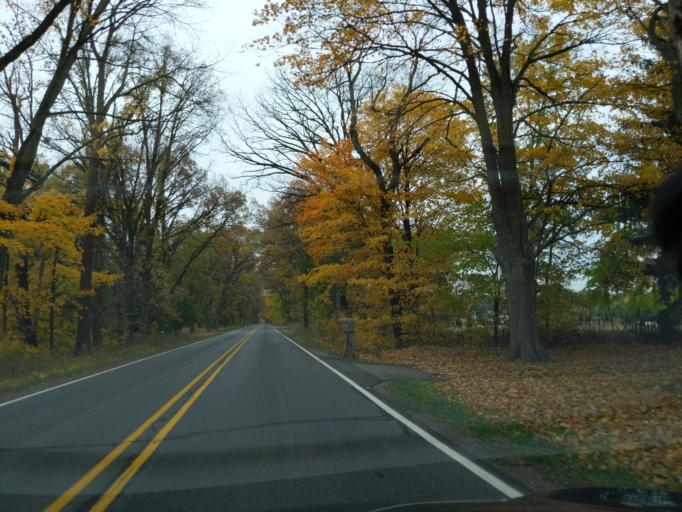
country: US
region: Michigan
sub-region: Jackson County
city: Spring Arbor
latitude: 42.2883
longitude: -84.6001
